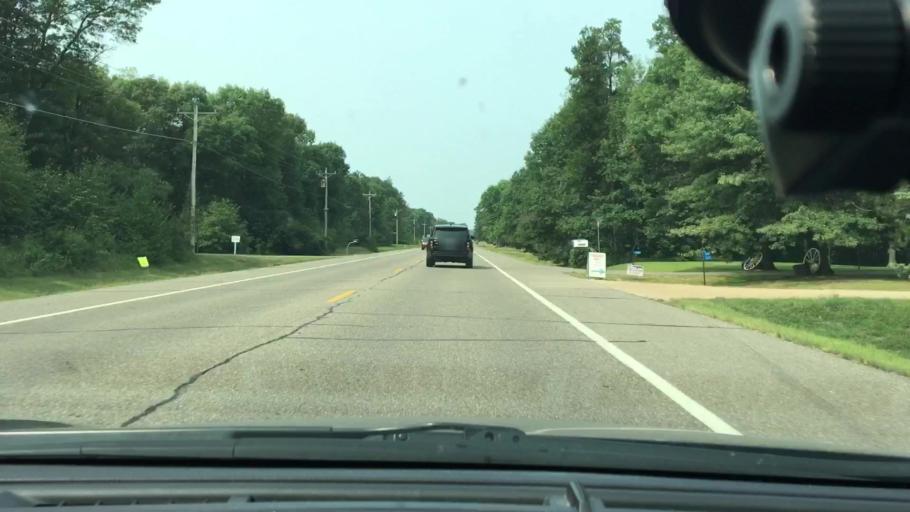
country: US
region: Minnesota
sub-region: Crow Wing County
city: Brainerd
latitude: 46.3985
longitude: -94.1986
